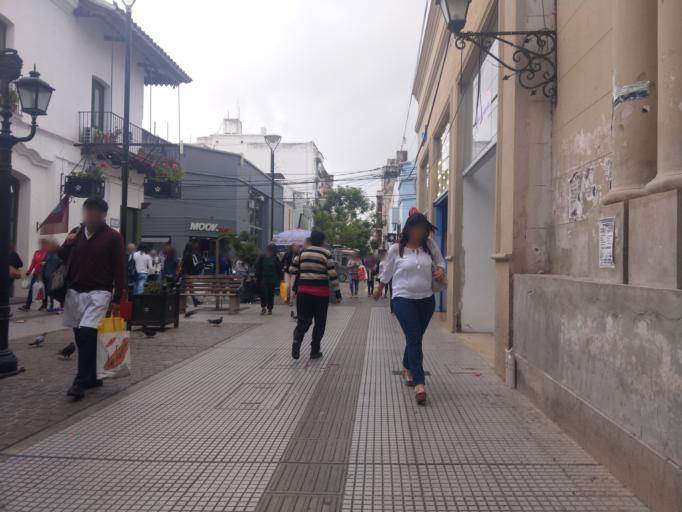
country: AR
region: Salta
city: Salta
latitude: -24.7906
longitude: -65.4125
